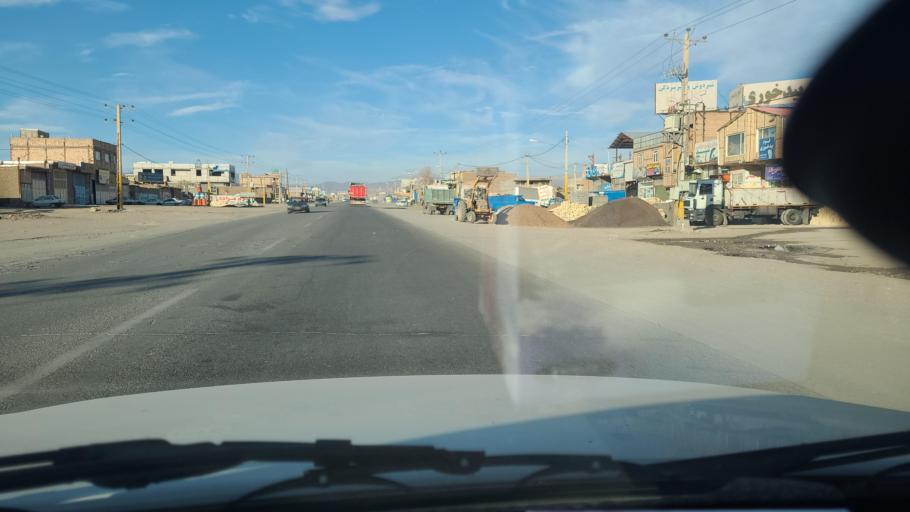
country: IR
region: Razavi Khorasan
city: Sabzevar
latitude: 36.2156
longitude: 57.6510
